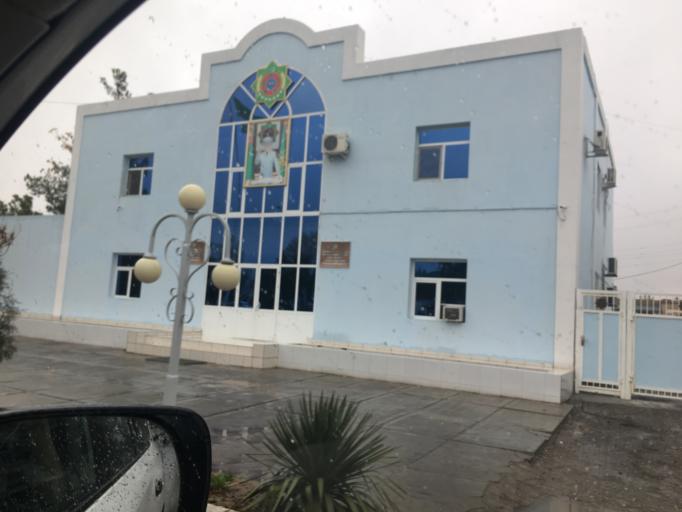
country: TM
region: Mary
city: Yoloeten
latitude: 37.2981
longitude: 62.3600
